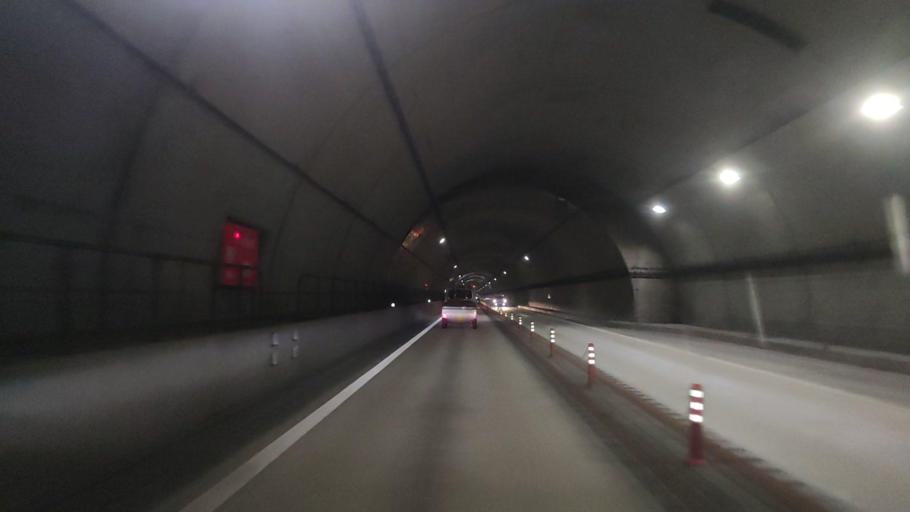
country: JP
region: Wakayama
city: Tanabe
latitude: 33.6165
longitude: 135.4226
